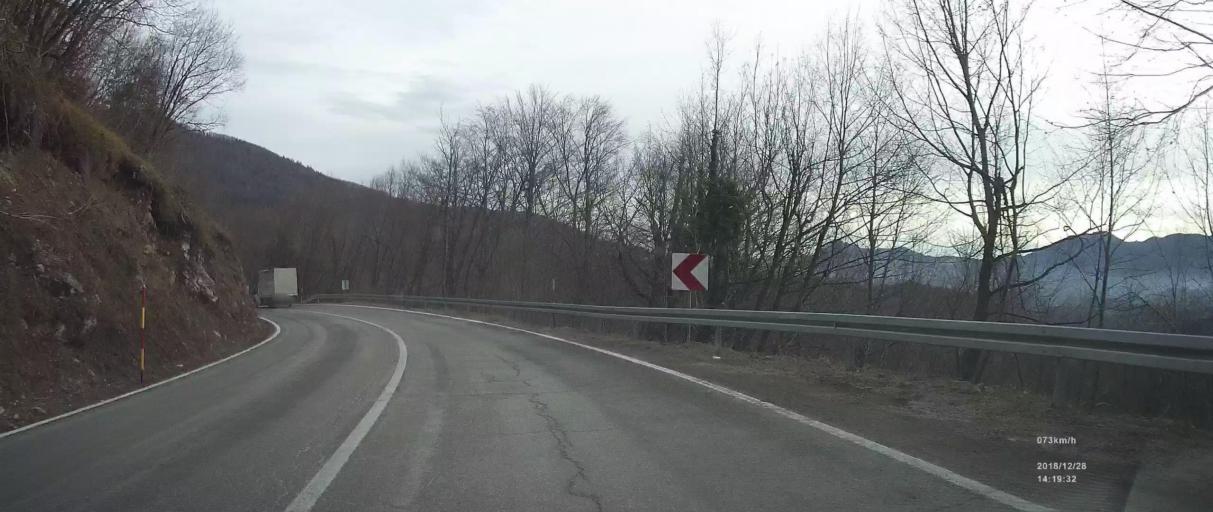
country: HR
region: Primorsko-Goranska
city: Vrbovsko
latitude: 45.4031
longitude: 15.0682
